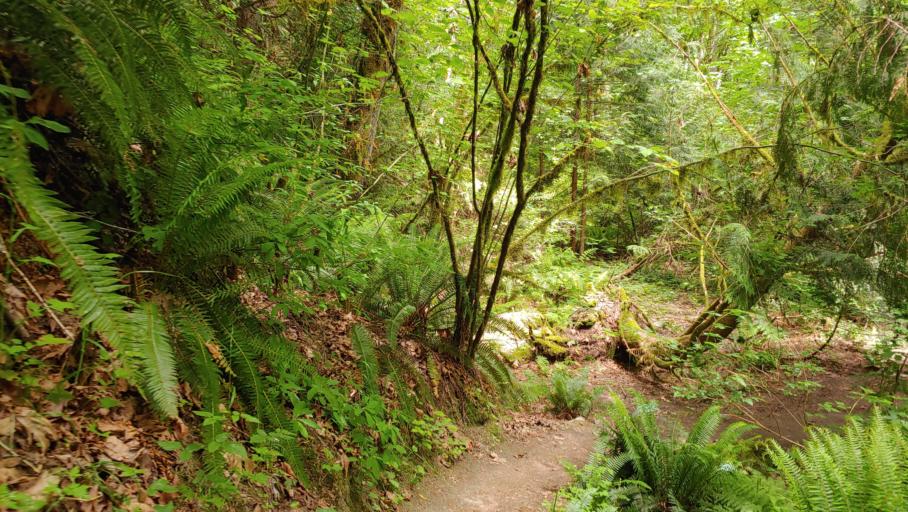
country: US
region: Washington
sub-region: King County
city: Newcastle
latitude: 47.5191
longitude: -122.1636
